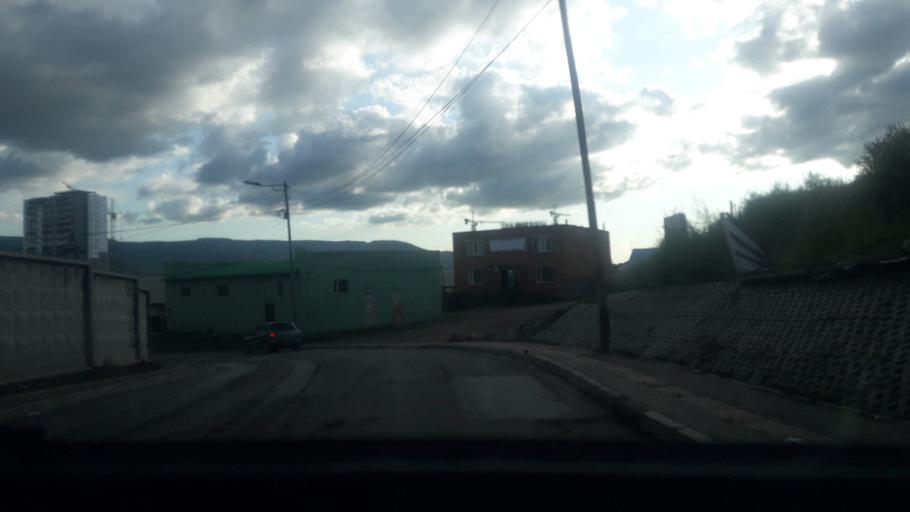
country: MN
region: Ulaanbaatar
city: Ulaanbaatar
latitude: 47.9174
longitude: 106.9949
